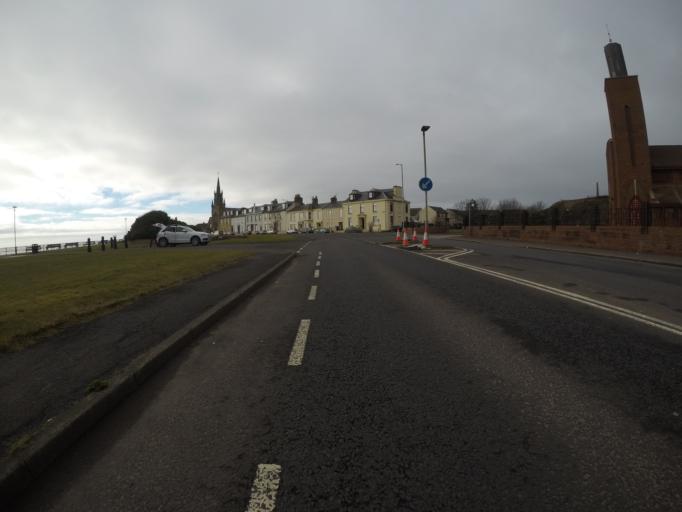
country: GB
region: Scotland
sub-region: North Ayrshire
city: Ardrossan
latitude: 55.6402
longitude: -4.8089
